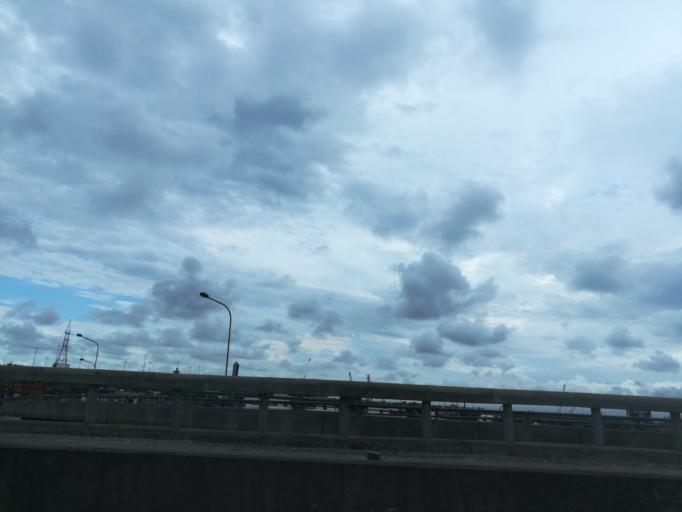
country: NG
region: Lagos
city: Lagos
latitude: 6.4648
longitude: 3.3858
